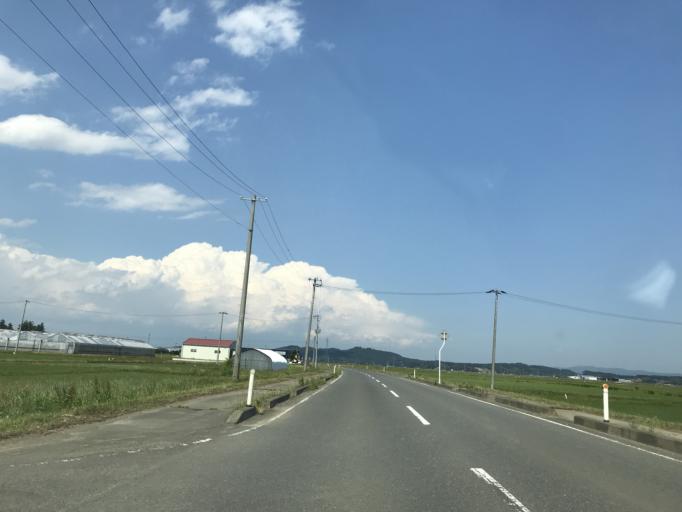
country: JP
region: Miyagi
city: Wakuya
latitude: 38.4602
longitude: 141.1237
